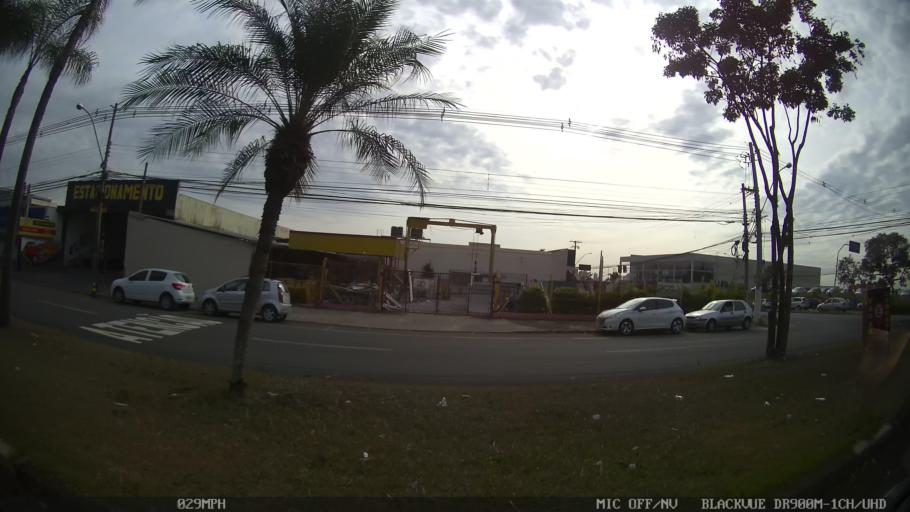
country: BR
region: Sao Paulo
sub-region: Piracicaba
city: Piracicaba
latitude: -22.7282
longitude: -47.6204
